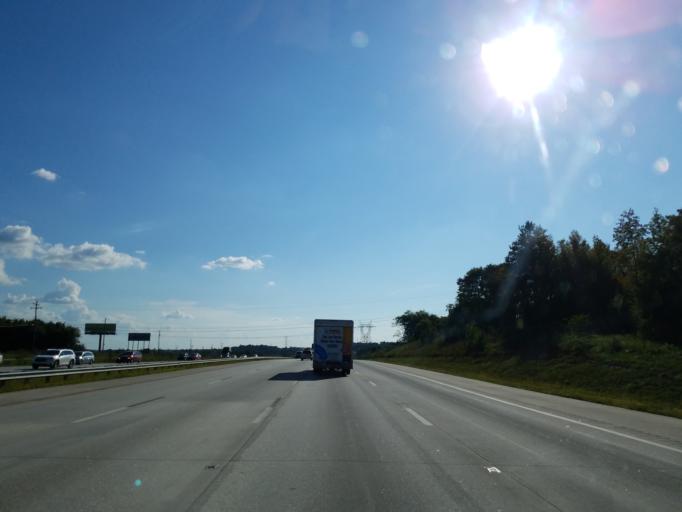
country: US
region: North Carolina
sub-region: Davidson County
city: Tyro
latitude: 35.7401
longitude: -80.3647
